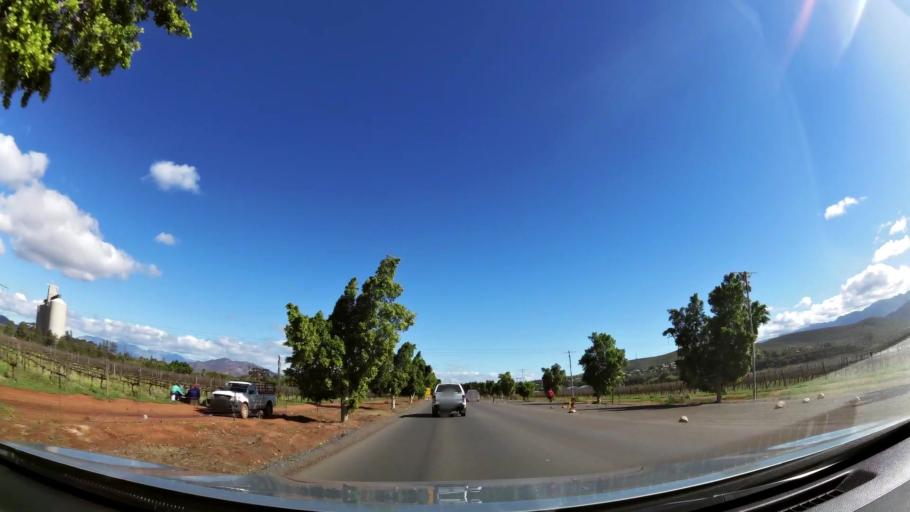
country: ZA
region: Western Cape
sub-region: Cape Winelands District Municipality
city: Ashton
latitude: -33.8318
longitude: 20.0734
